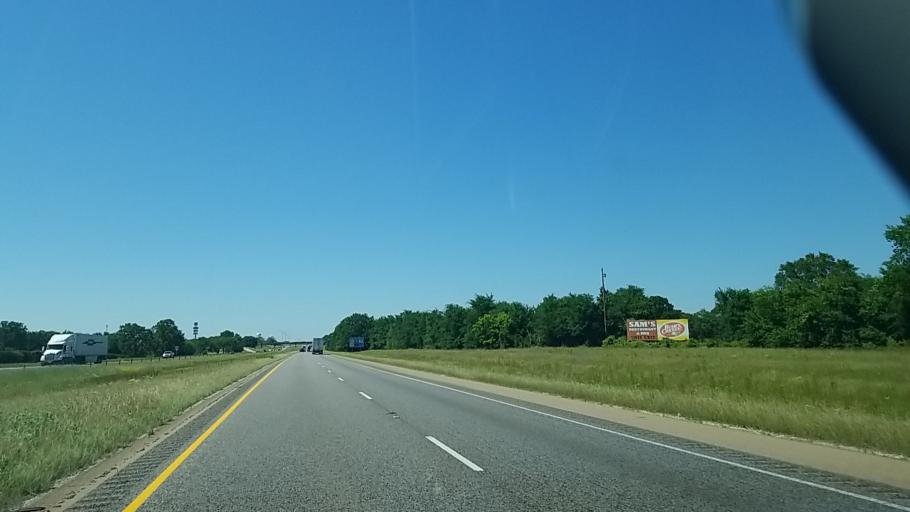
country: US
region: Texas
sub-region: Freestone County
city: Fairfield
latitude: 31.7053
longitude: -96.1734
